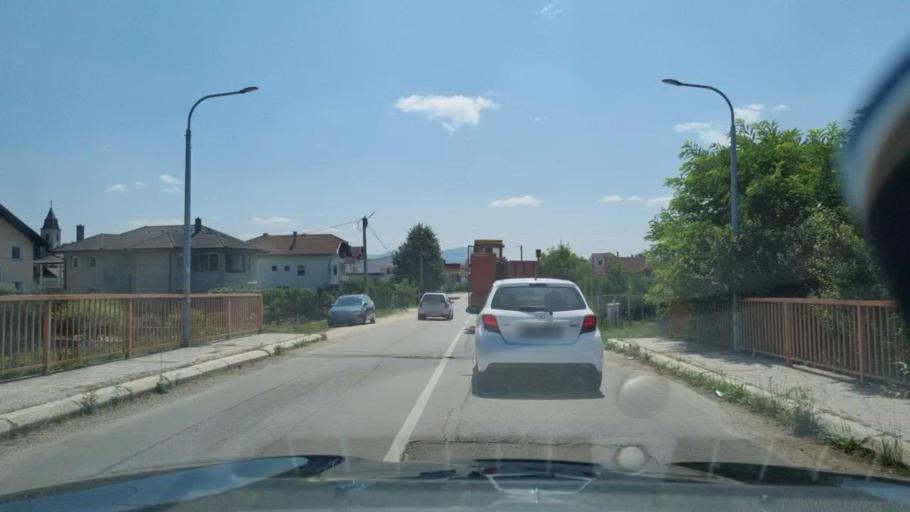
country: BA
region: Federation of Bosnia and Herzegovina
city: Sanski Most
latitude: 44.7697
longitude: 16.6696
